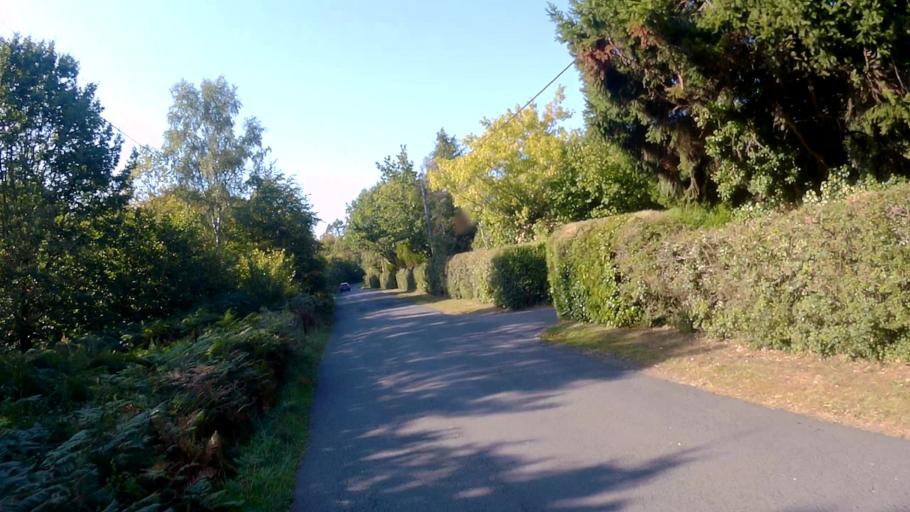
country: GB
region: England
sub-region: Hampshire
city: Lindford
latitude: 51.1621
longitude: -0.8380
